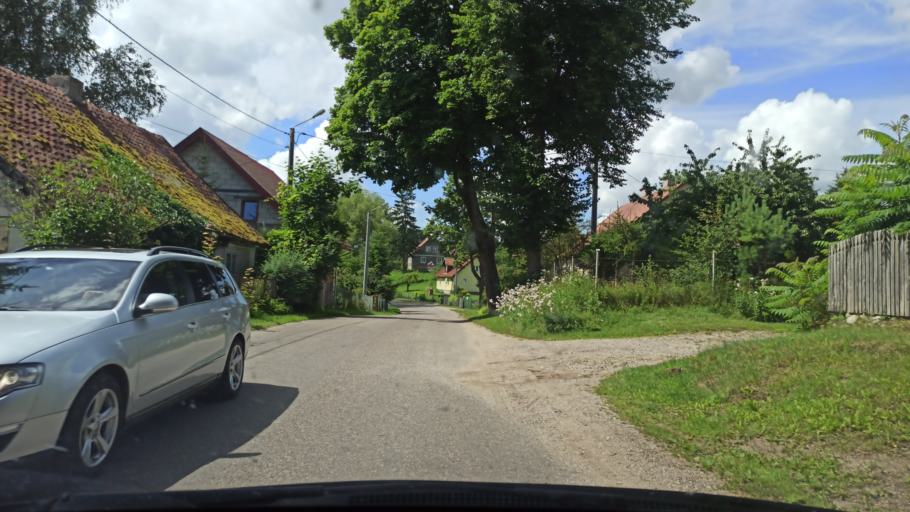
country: PL
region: Warmian-Masurian Voivodeship
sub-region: Powiat ostrodzki
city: Morag
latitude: 53.8671
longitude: 20.0117
